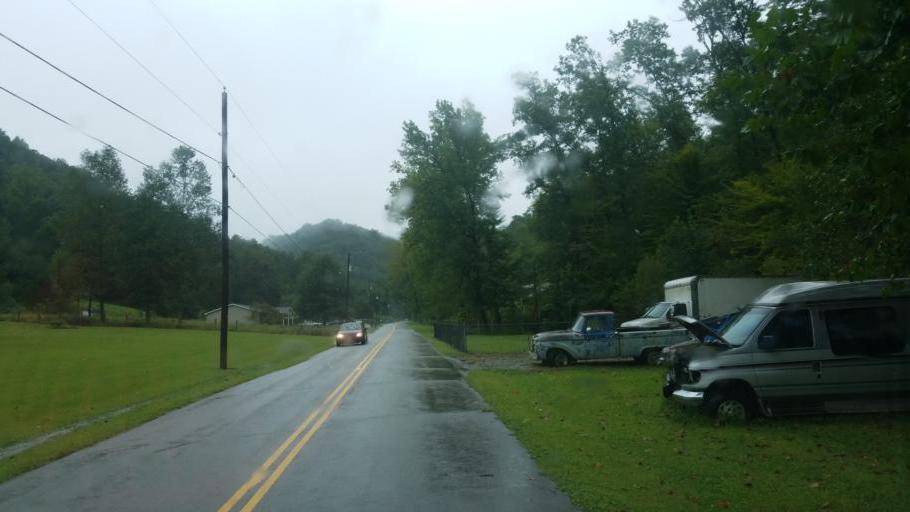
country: US
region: Ohio
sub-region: Scioto County
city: West Portsmouth
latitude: 38.7501
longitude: -83.0980
